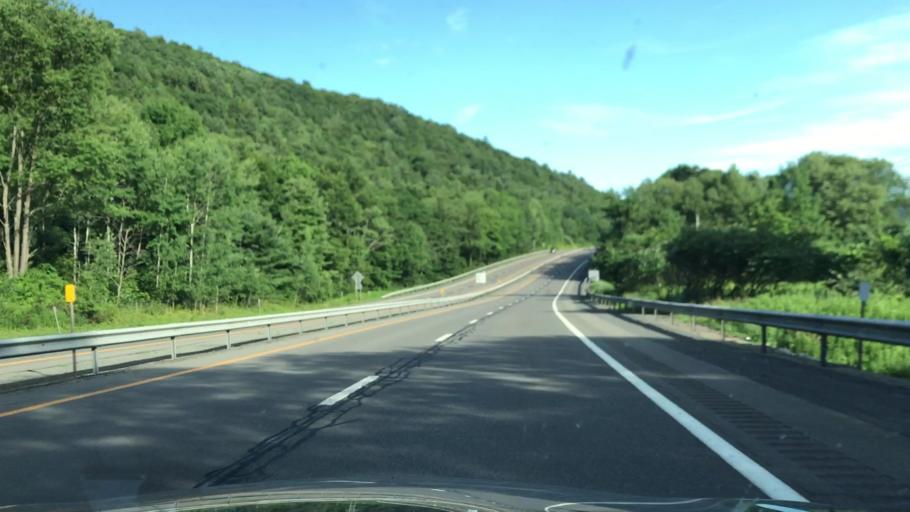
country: US
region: New York
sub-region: Delaware County
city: Hancock
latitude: 41.9641
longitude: -75.3208
